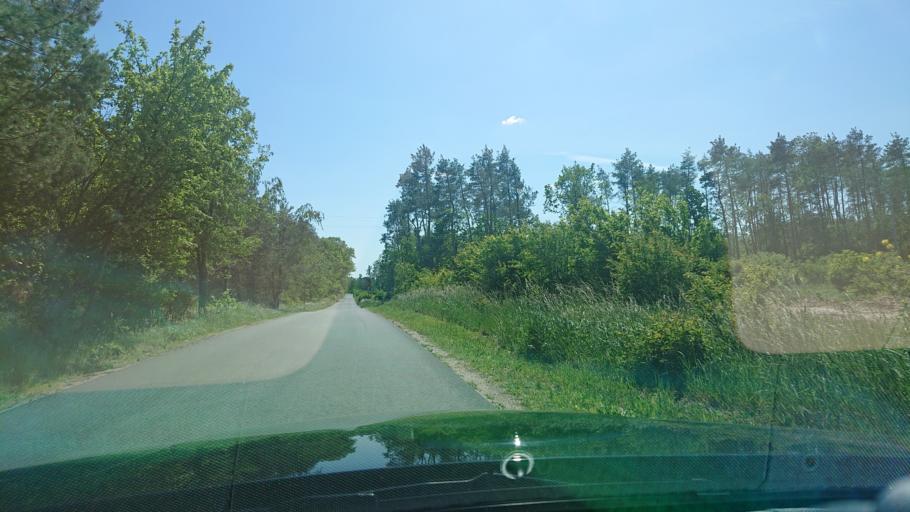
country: PL
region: Greater Poland Voivodeship
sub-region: Powiat gnieznienski
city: Gniezno
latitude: 52.4972
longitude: 17.5817
